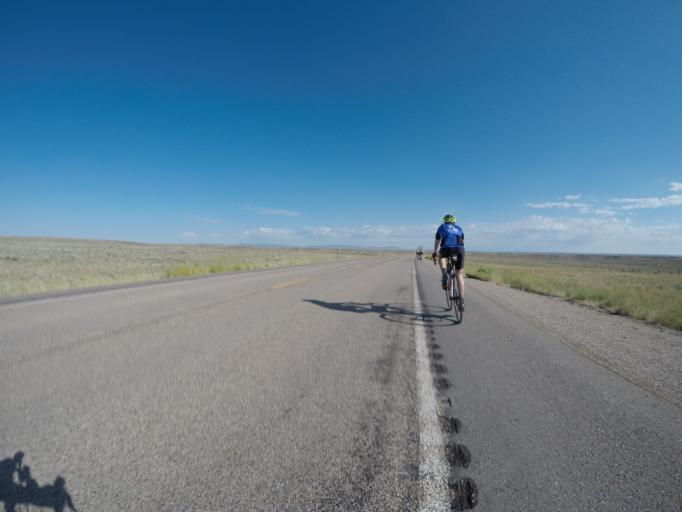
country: US
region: Wyoming
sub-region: Lincoln County
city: Kemmerer
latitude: 42.0359
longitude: -110.1560
